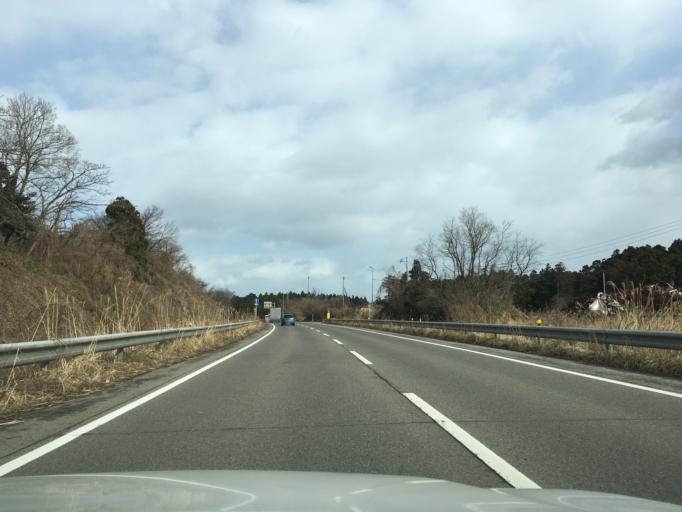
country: JP
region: Yamagata
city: Yuza
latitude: 39.2581
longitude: 139.9265
